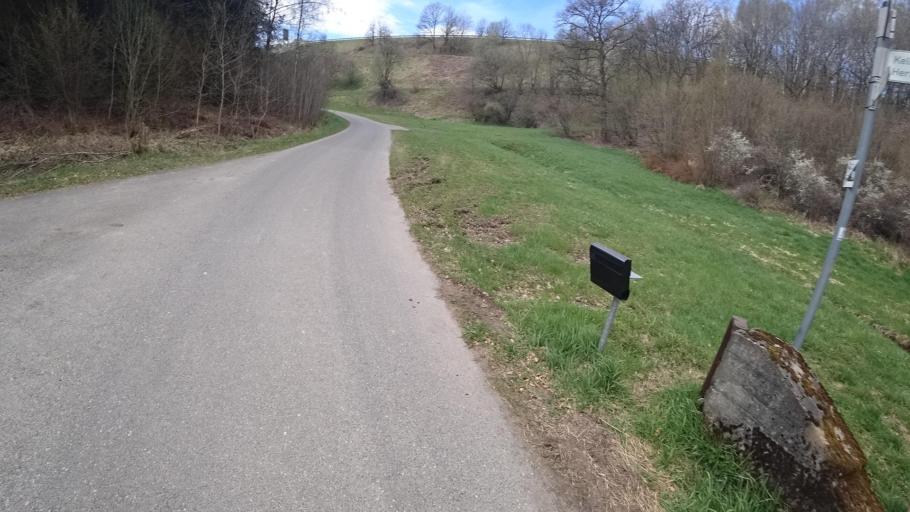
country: DE
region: Rheinland-Pfalz
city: Hermeskeil
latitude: 49.6478
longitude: 6.9292
